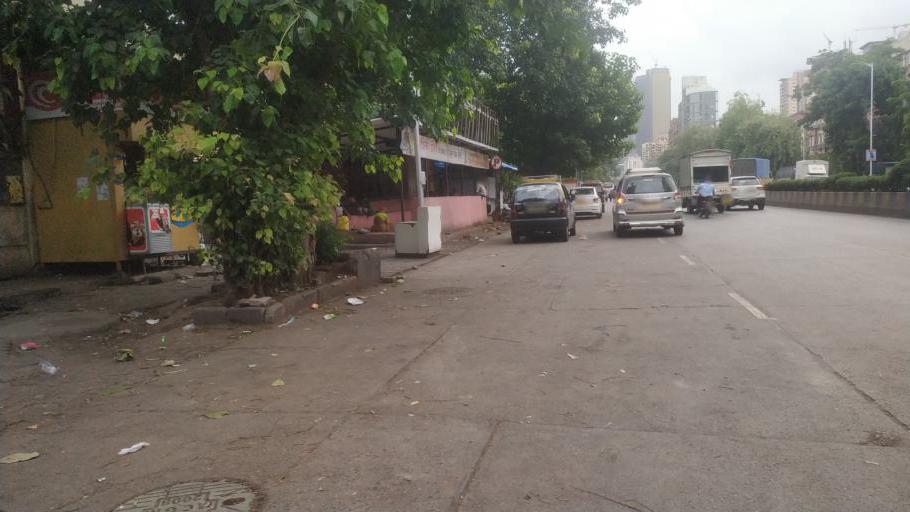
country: IN
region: Maharashtra
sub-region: Mumbai Suburban
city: Mumbai
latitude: 19.0151
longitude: 72.8391
